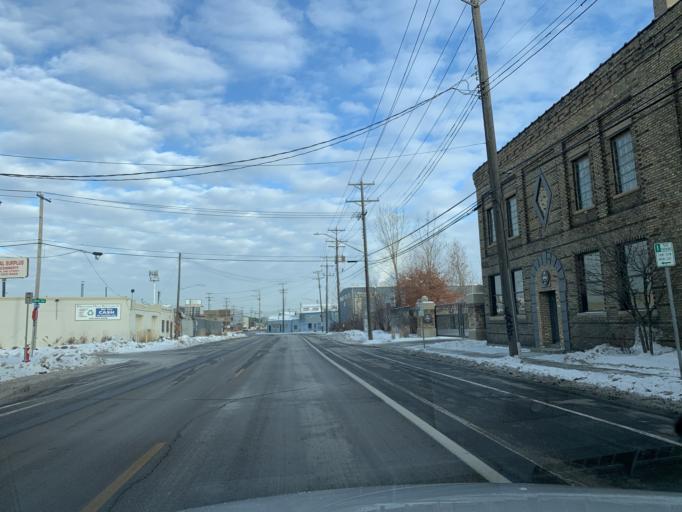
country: US
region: Minnesota
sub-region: Hennepin County
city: Minneapolis
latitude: 44.9971
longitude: -93.2800
